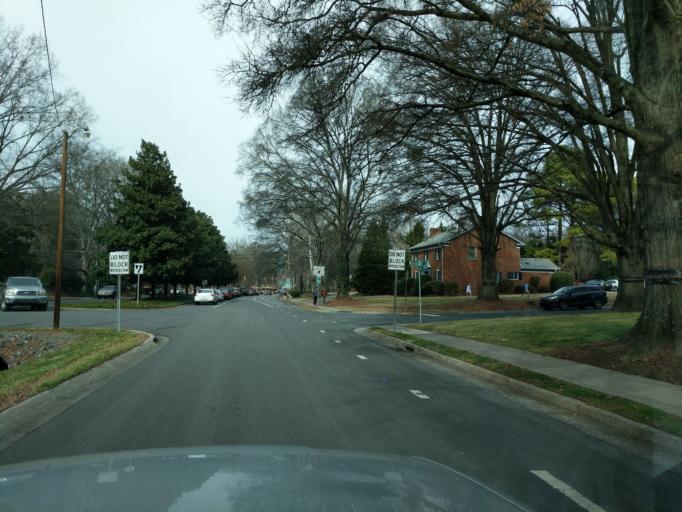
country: US
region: North Carolina
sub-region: Mecklenburg County
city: Charlotte
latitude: 35.1641
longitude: -80.8287
